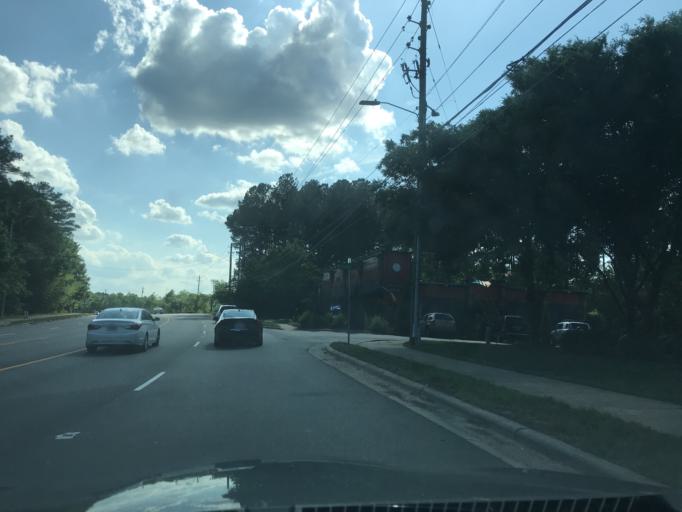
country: US
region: North Carolina
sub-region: Wake County
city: West Raleigh
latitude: 35.8939
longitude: -78.6235
